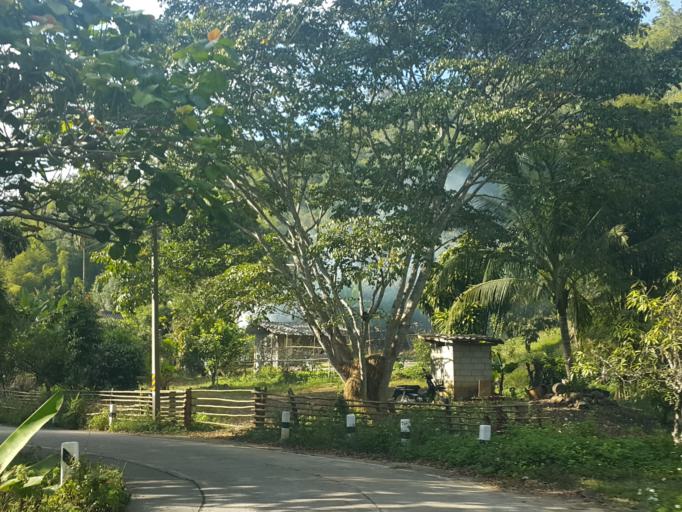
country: TH
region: Chiang Mai
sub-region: Amphoe Chiang Dao
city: Chiang Dao
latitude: 19.4124
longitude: 98.9213
